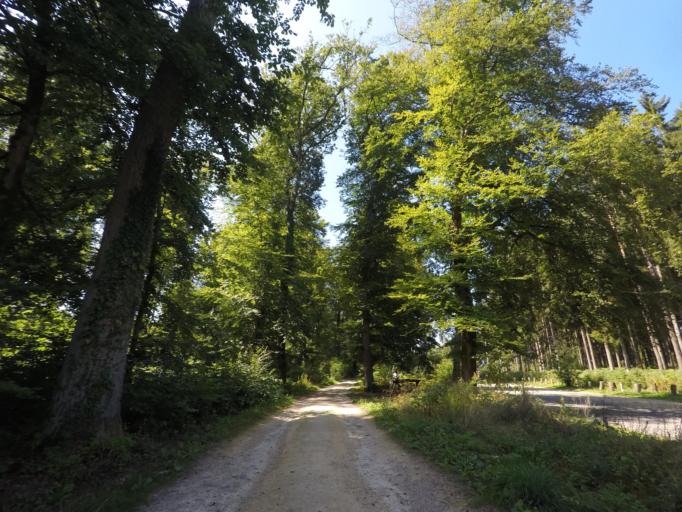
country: LU
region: Luxembourg
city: Bereldange
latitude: 49.6483
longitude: 6.1100
